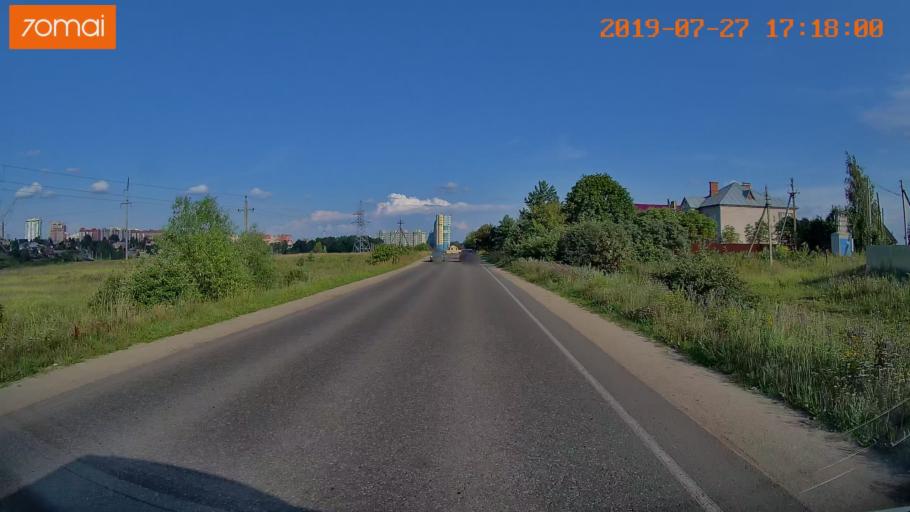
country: RU
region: Ivanovo
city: Novo-Talitsy
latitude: 57.0331
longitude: 40.9014
